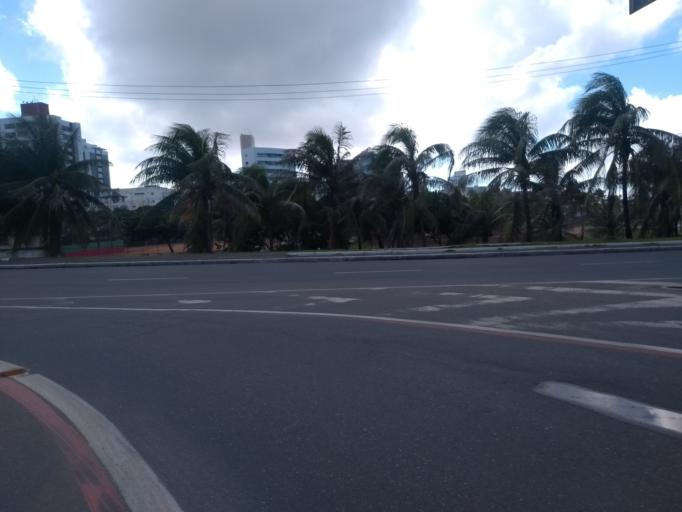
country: BR
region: Bahia
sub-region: Salvador
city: Salvador
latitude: -12.9990
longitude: -38.4496
